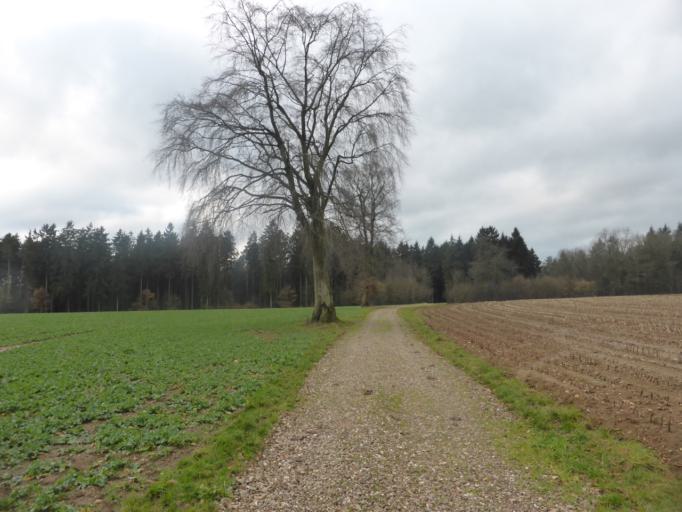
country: LU
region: Diekirch
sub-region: Canton de Redange
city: Grosbous
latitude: 49.8333
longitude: 5.9401
